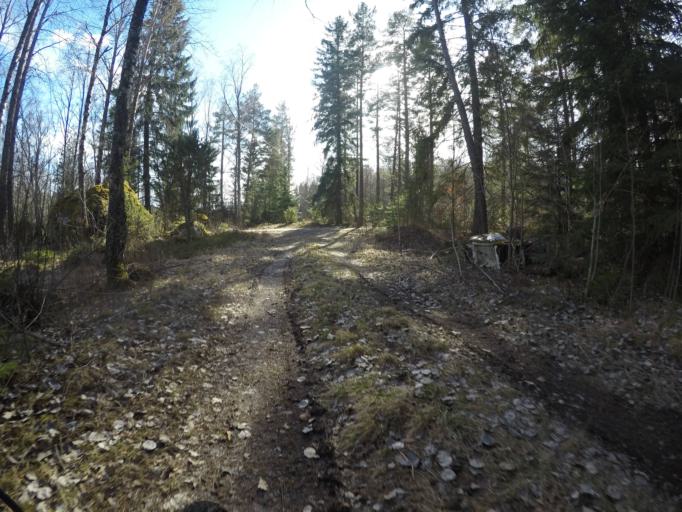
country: SE
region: Soedermanland
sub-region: Eskilstuna Kommun
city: Kvicksund
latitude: 59.4242
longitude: 16.2847
